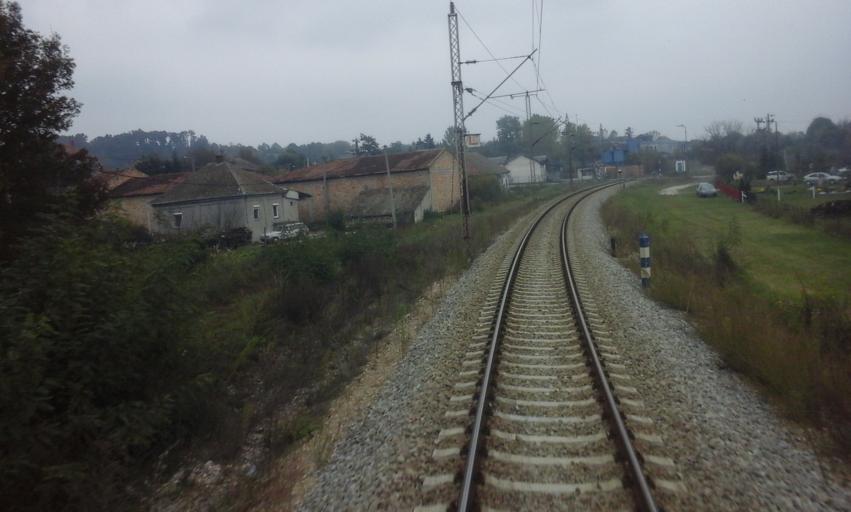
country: RS
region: Central Serbia
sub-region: Belgrade
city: Mladenovac
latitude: 44.4772
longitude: 20.6629
